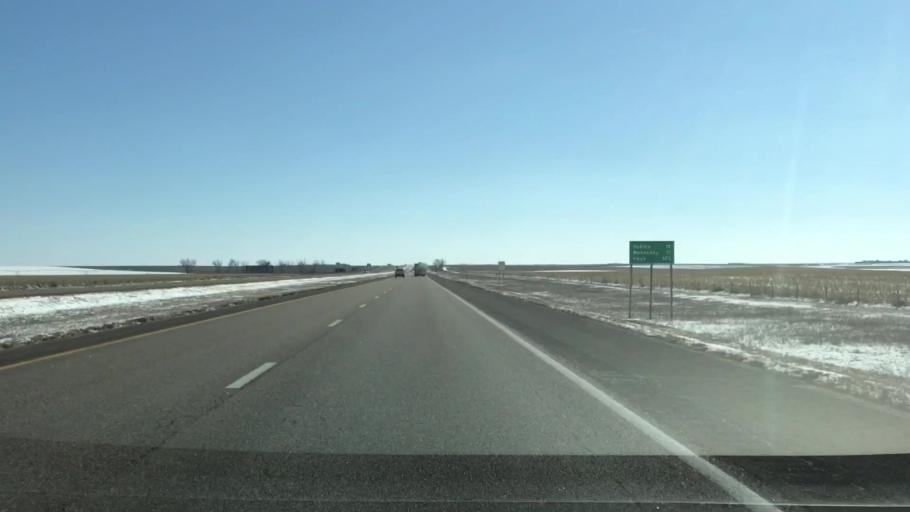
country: US
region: Kansas
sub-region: Thomas County
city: Colby
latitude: 39.3561
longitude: -101.0253
